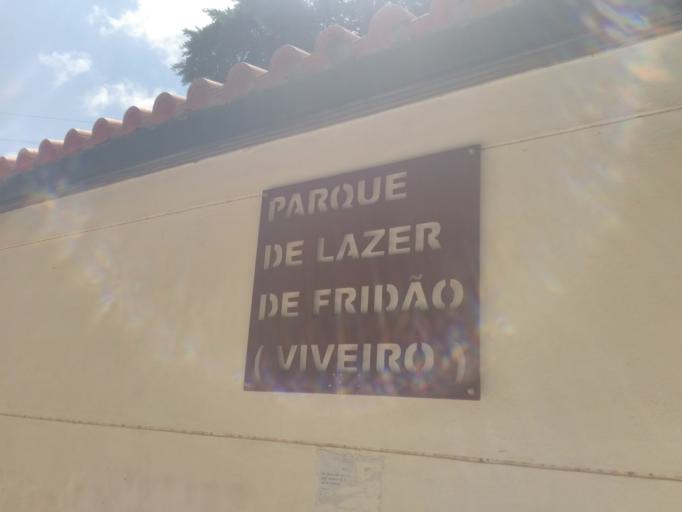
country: PT
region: Braga
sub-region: Celorico de Basto
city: Celorico de Basto
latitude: 41.3126
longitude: -8.0132
